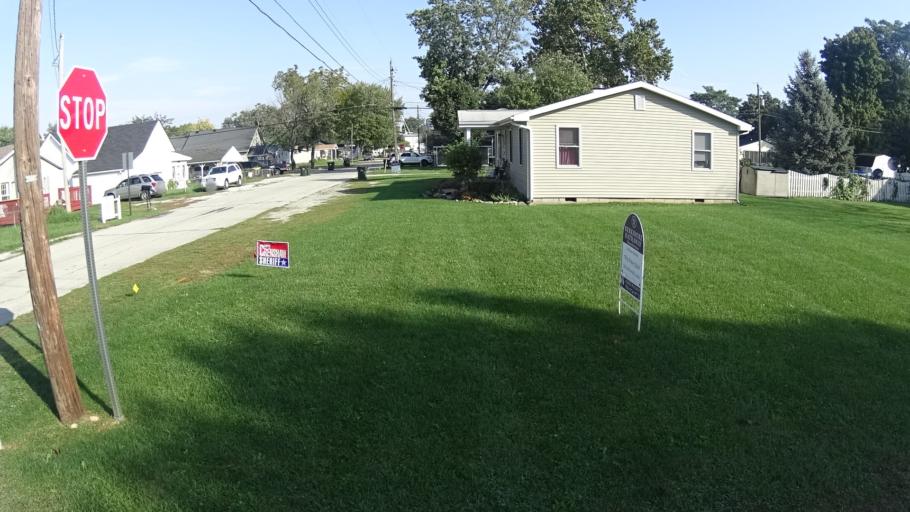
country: US
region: Indiana
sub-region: Madison County
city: Lapel
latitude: 40.0646
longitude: -85.8503
